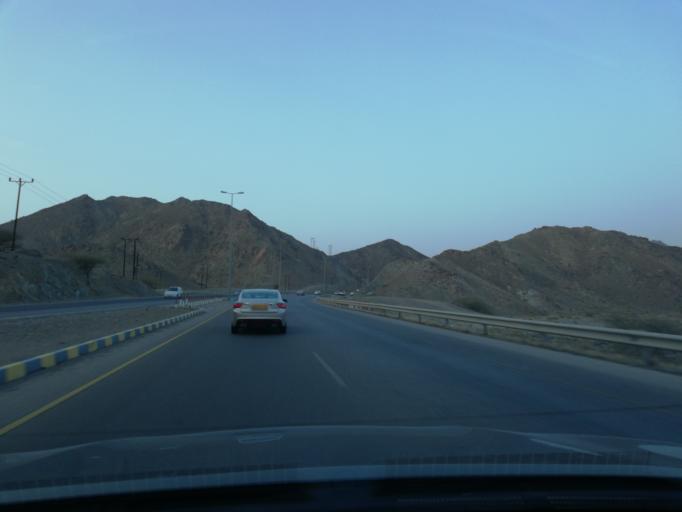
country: OM
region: Muhafazat ad Dakhiliyah
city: Bidbid
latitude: 23.4658
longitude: 58.1890
